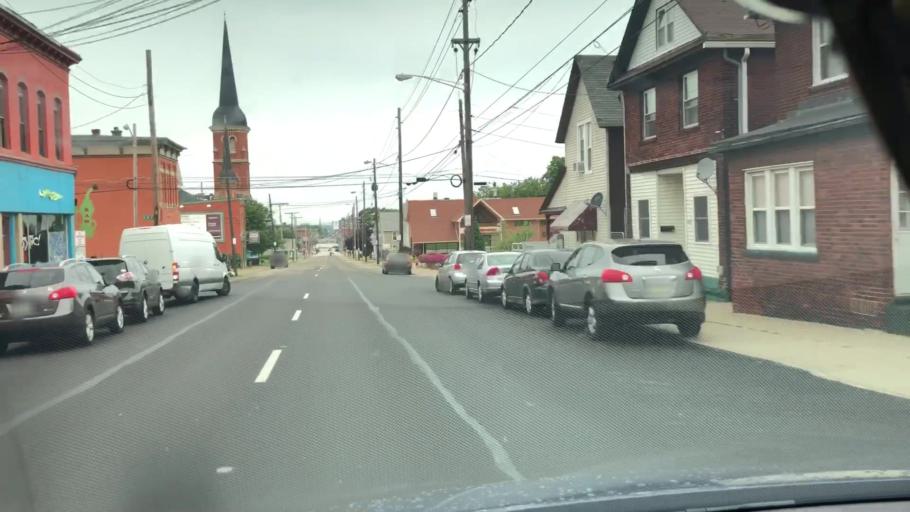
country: US
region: Pennsylvania
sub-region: Erie County
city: Erie
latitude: 42.1128
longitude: -80.0758
